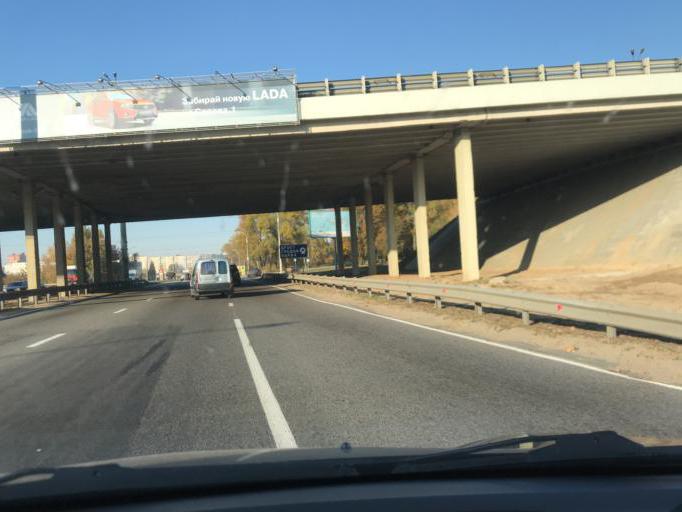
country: BY
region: Minsk
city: Syenitsa
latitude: 53.8349
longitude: 27.5335
